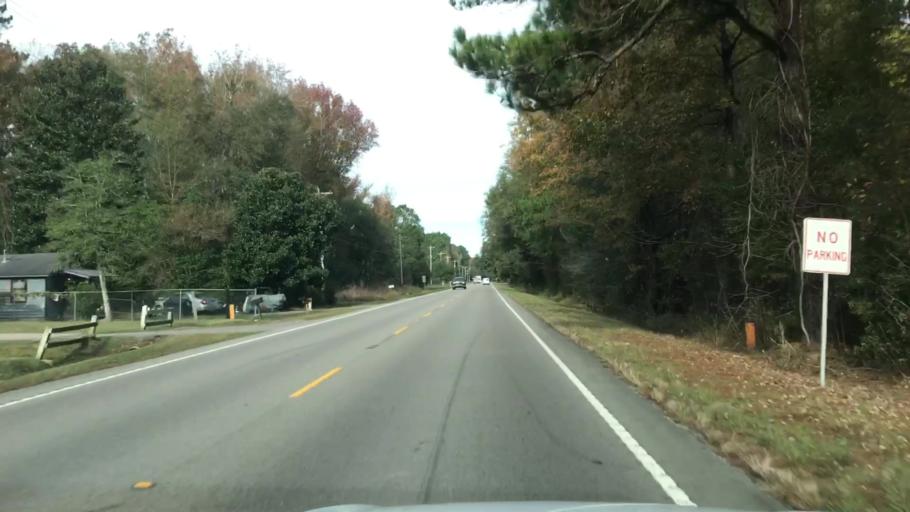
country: US
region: South Carolina
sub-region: Colleton County
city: Walterboro
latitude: 32.8269
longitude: -80.5619
